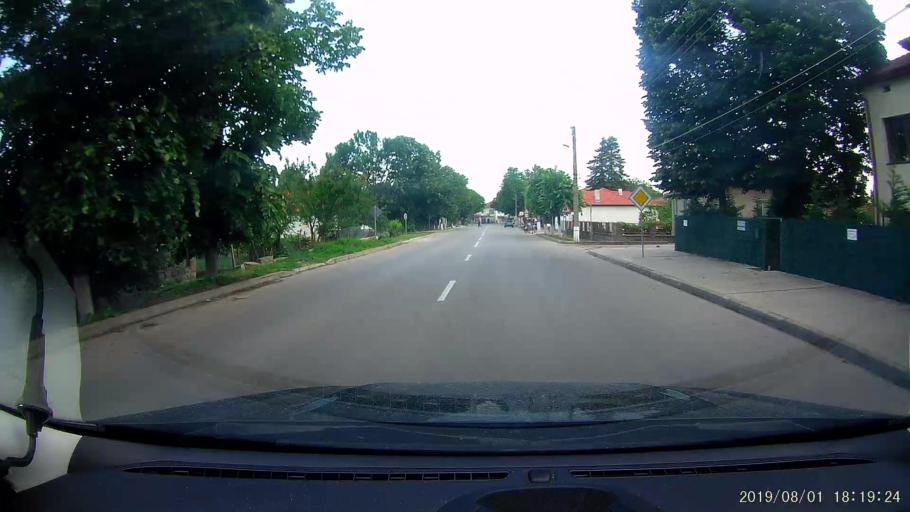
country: BG
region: Shumen
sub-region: Obshtina Kaolinovo
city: Kaolinovo
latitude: 43.6839
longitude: 27.0906
